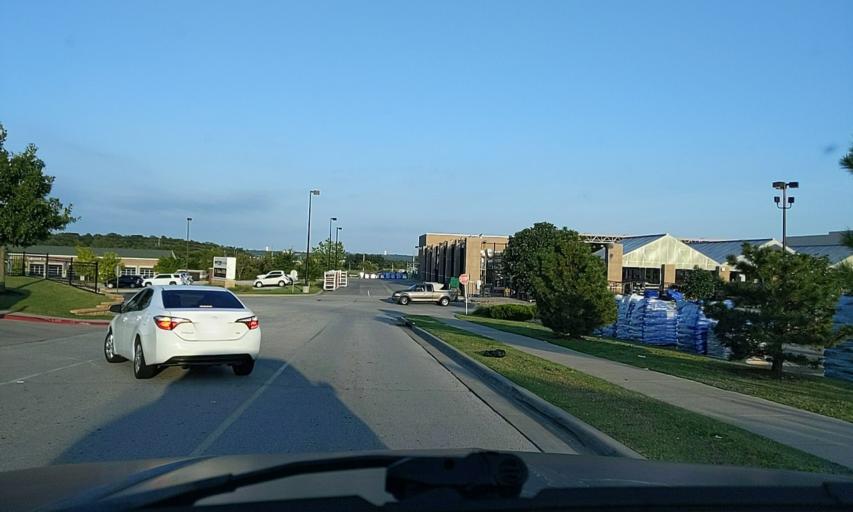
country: US
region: Oklahoma
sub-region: Tulsa County
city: Jenks
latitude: 36.0600
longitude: -96.0025
